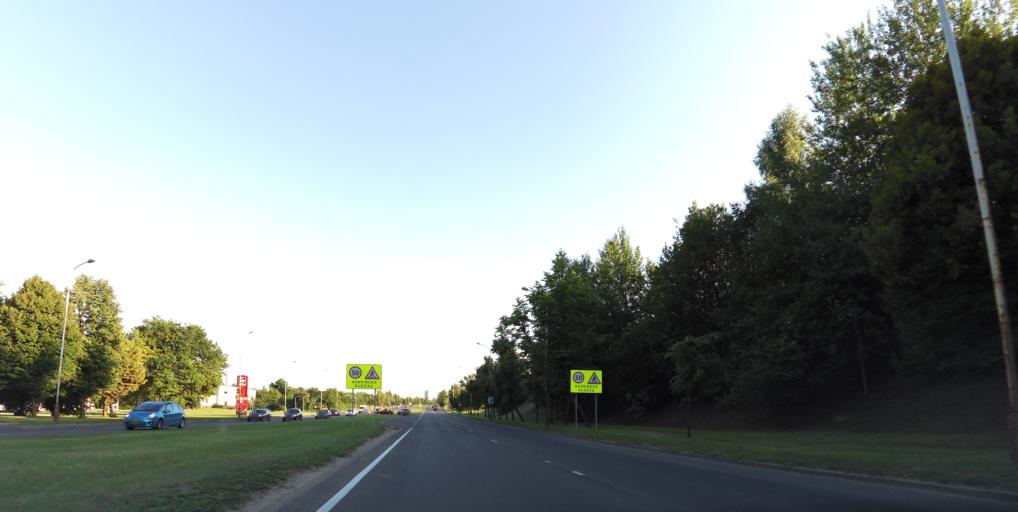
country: LT
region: Vilnius County
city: Seskine
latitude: 54.7234
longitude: 25.2695
